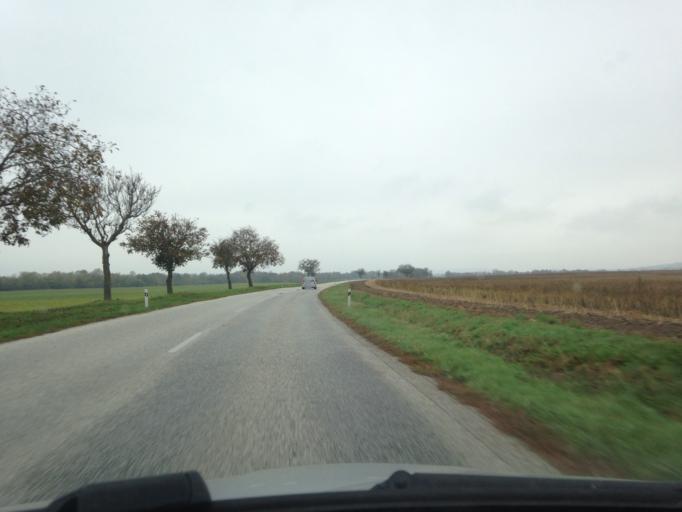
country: HU
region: Komarom-Esztergom
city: Nyergesujfalu
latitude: 47.8196
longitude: 18.5774
